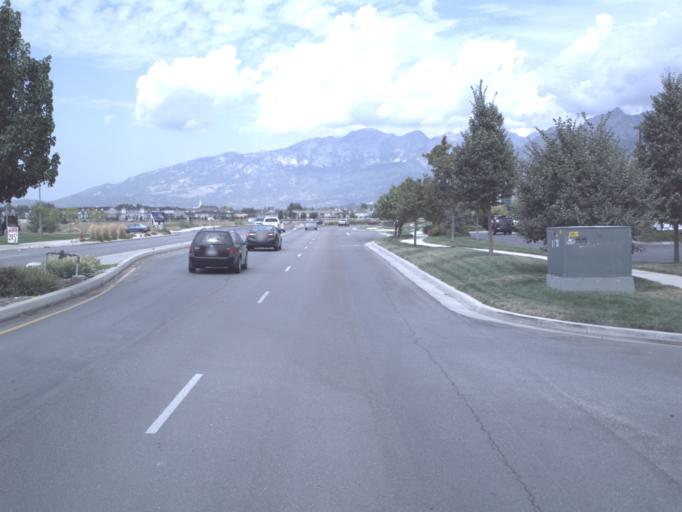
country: US
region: Utah
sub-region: Utah County
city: Pleasant Grove
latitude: 40.3561
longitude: -111.7633
